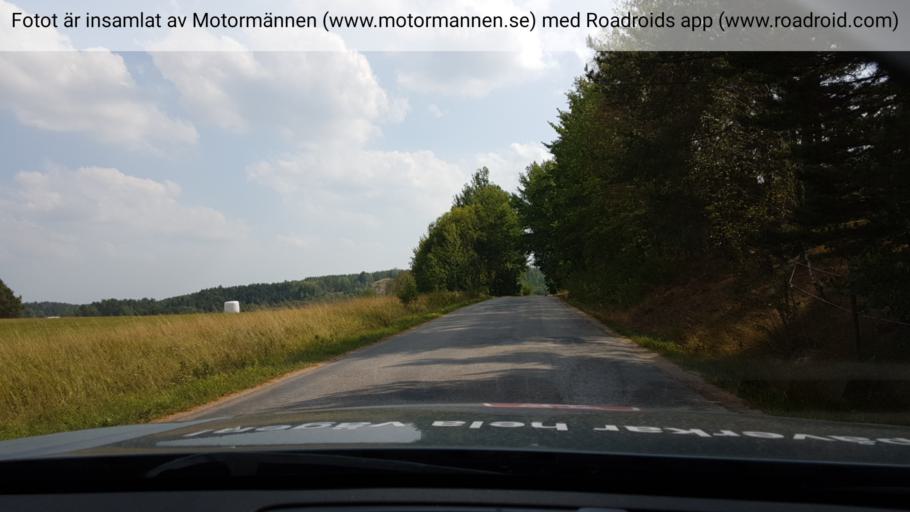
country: SE
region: Soedermanland
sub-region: Gnesta Kommun
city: Gnesta
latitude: 59.0443
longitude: 17.2712
